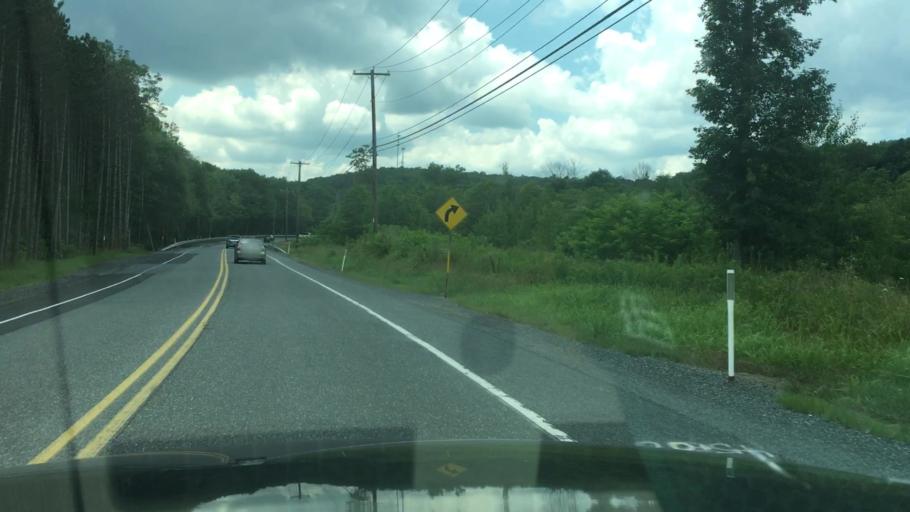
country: US
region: Pennsylvania
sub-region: Schuylkill County
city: Ashland
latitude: 40.7100
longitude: -76.3327
